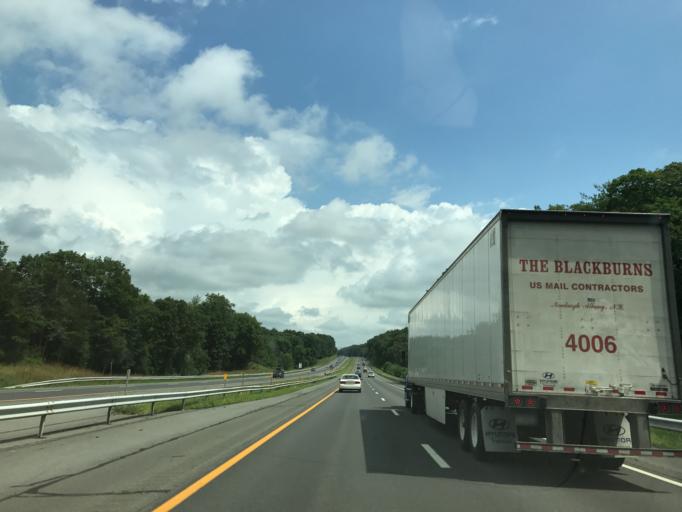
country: US
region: New York
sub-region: Greene County
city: Jefferson Heights
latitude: 42.3078
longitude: -73.8716
